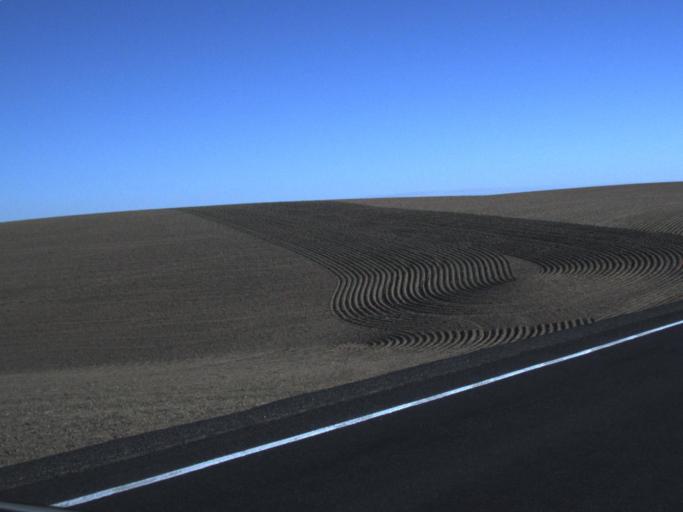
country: US
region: Washington
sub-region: Adams County
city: Ritzville
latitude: 47.0071
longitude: -118.3496
